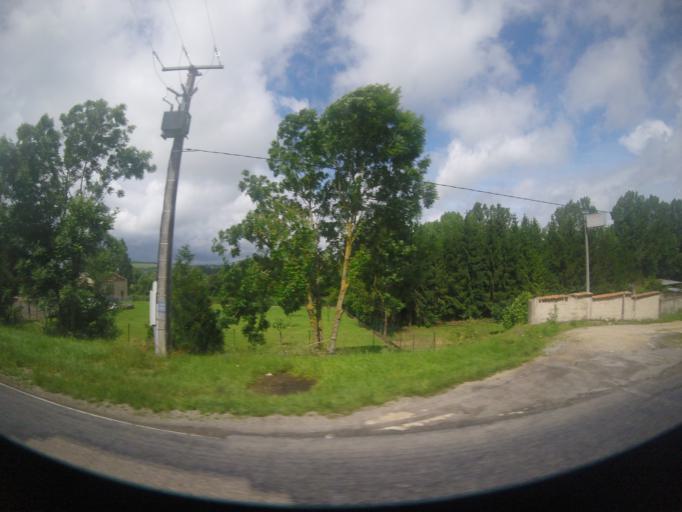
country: FR
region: Lorraine
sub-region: Departement de la Meuse
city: Dugny-sur-Meuse
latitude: 49.1153
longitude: 5.4152
